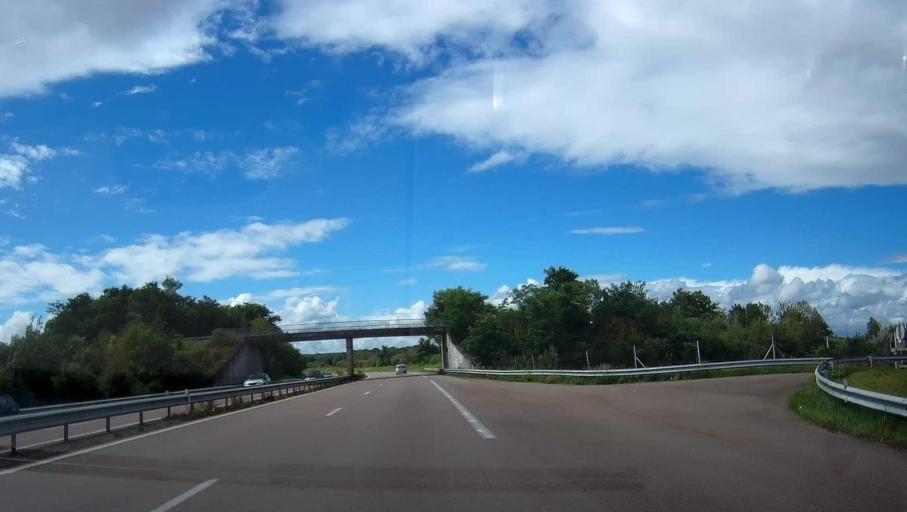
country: FR
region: Bourgogne
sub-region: Departement de la Cote-d'Or
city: Fenay
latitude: 47.2467
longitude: 5.0655
